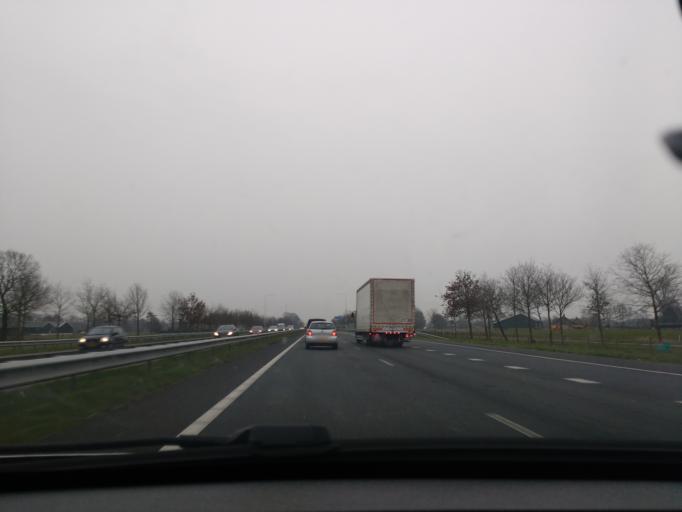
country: NL
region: Gelderland
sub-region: Gemeente Ede
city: Lunteren
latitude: 52.0594
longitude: 5.6137
